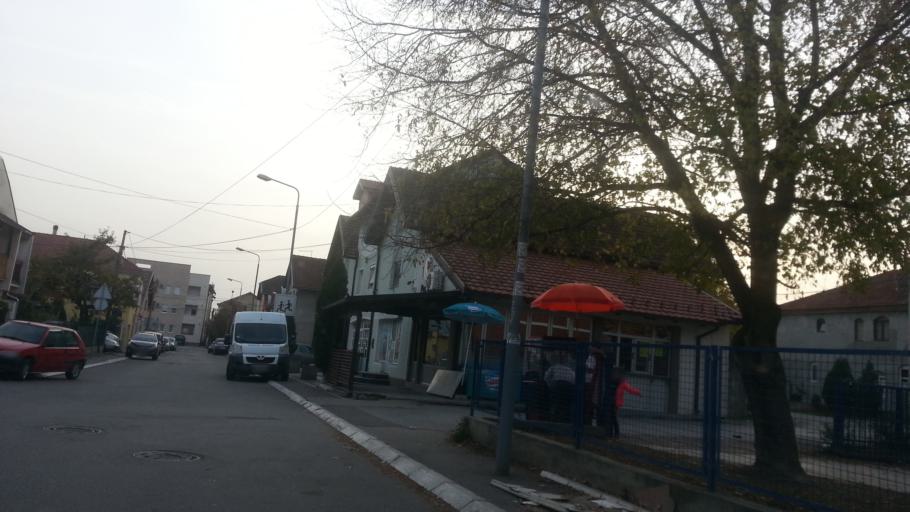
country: RS
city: Novi Banovci
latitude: 44.8999
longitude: 20.2818
